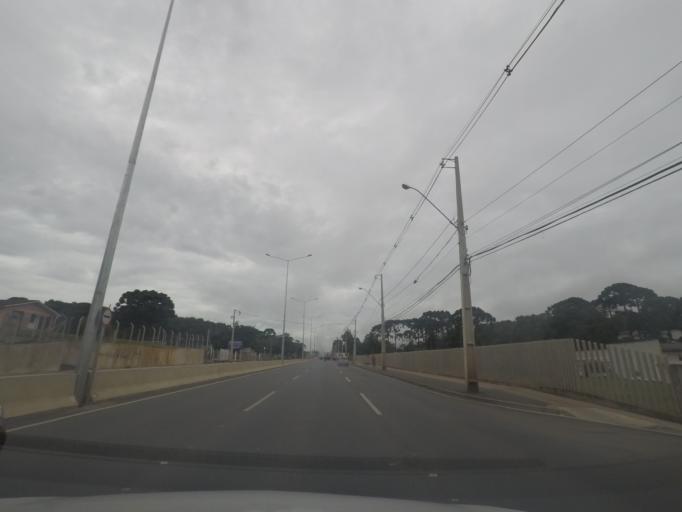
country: BR
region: Parana
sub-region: Piraquara
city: Piraquara
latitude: -25.4553
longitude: -49.1096
